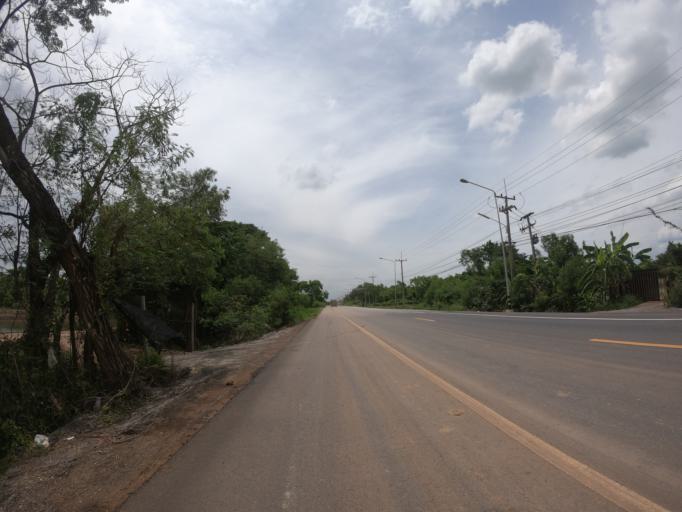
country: TH
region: Pathum Thani
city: Nong Suea
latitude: 14.0416
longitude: 100.8701
